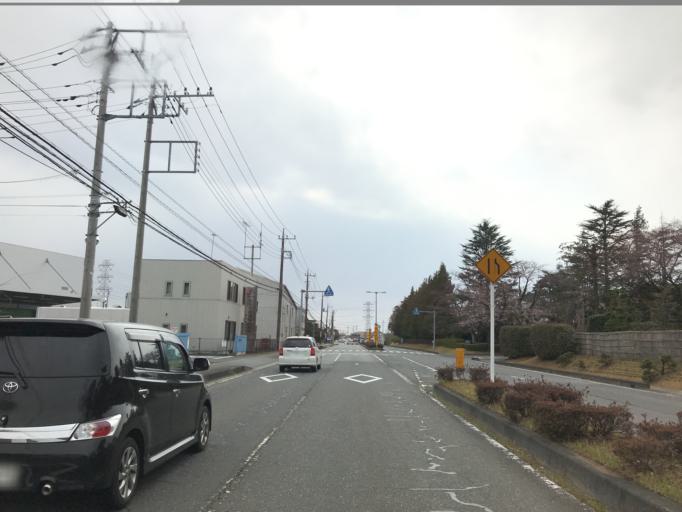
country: JP
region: Ibaraki
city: Ushiku
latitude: 35.9942
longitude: 140.0651
